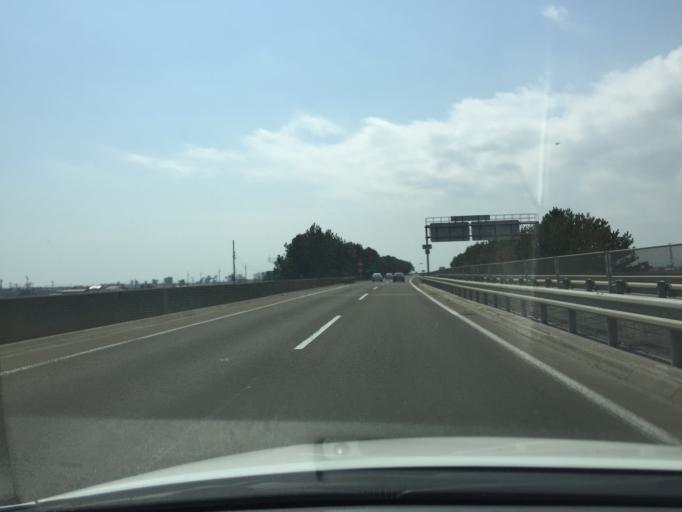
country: JP
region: Miyagi
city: Sendai
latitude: 38.1958
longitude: 140.9413
